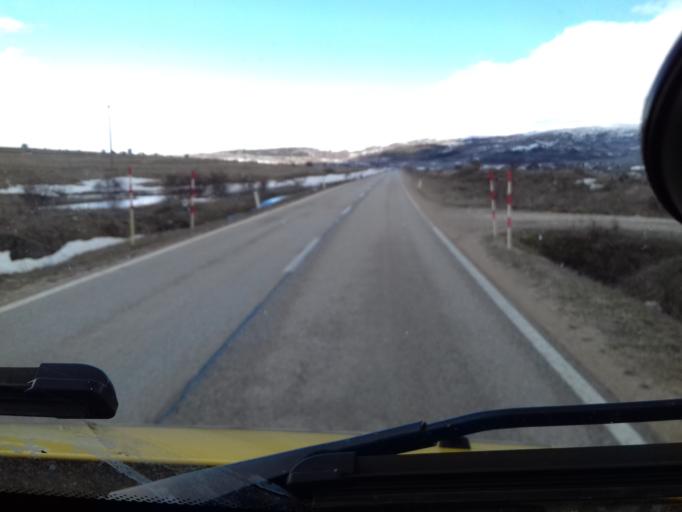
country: BA
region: Federation of Bosnia and Herzegovina
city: Tomislavgrad
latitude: 43.7421
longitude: 17.2255
